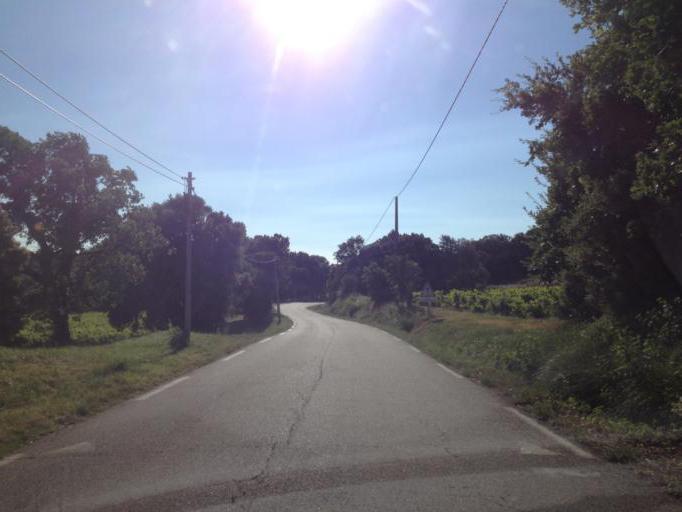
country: FR
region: Provence-Alpes-Cote d'Azur
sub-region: Departement du Vaucluse
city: Chateauneuf-du-Pape
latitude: 44.0519
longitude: 4.8552
